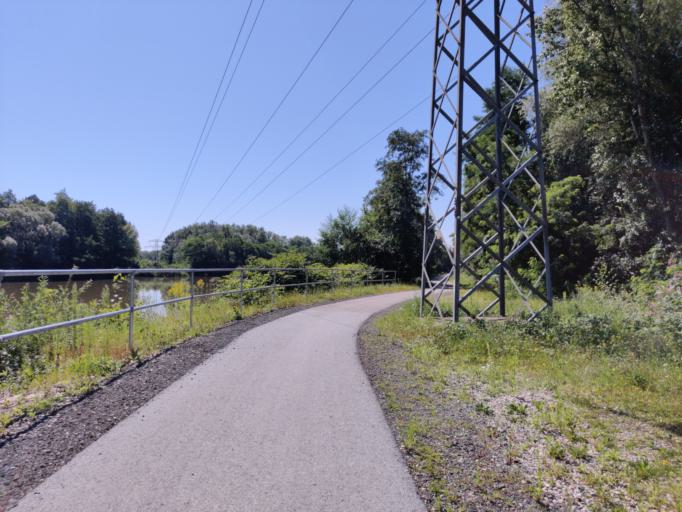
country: AT
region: Styria
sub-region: Politischer Bezirk Leibnitz
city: Stocking
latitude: 46.8739
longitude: 15.5312
